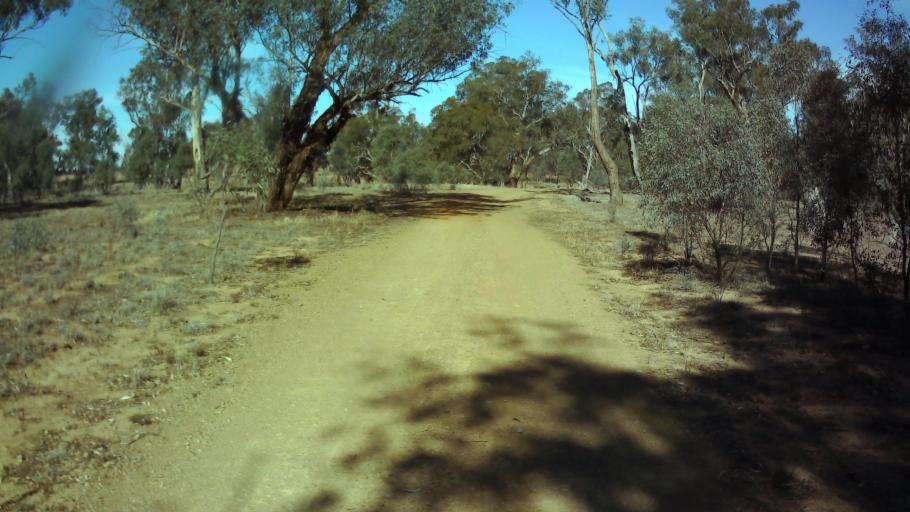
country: AU
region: New South Wales
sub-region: Weddin
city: Grenfell
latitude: -33.7336
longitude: 148.0916
